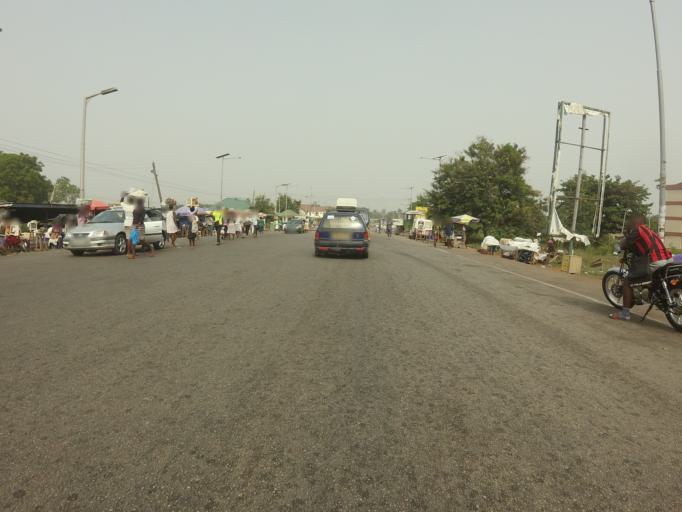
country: GH
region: Volta
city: Anloga
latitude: 5.9967
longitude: 0.5880
